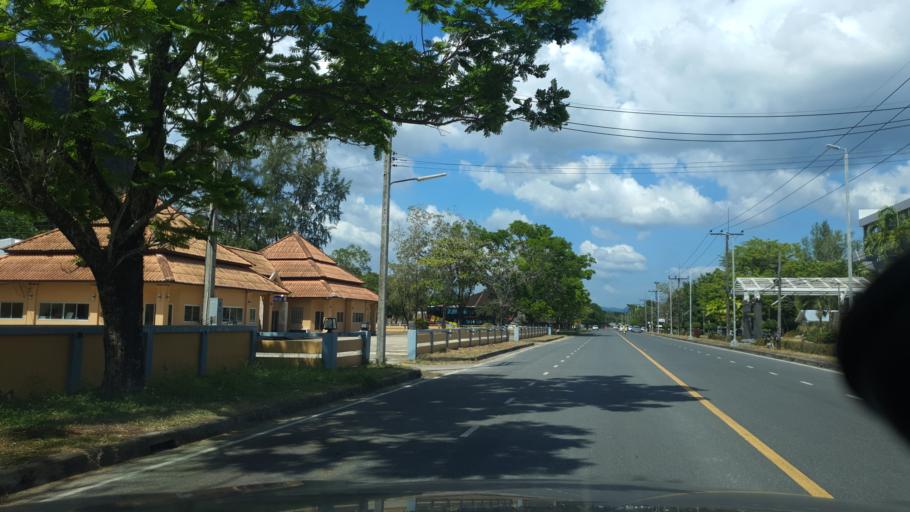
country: TH
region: Phangnga
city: Phang Nga
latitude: 8.3988
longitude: 98.5134
